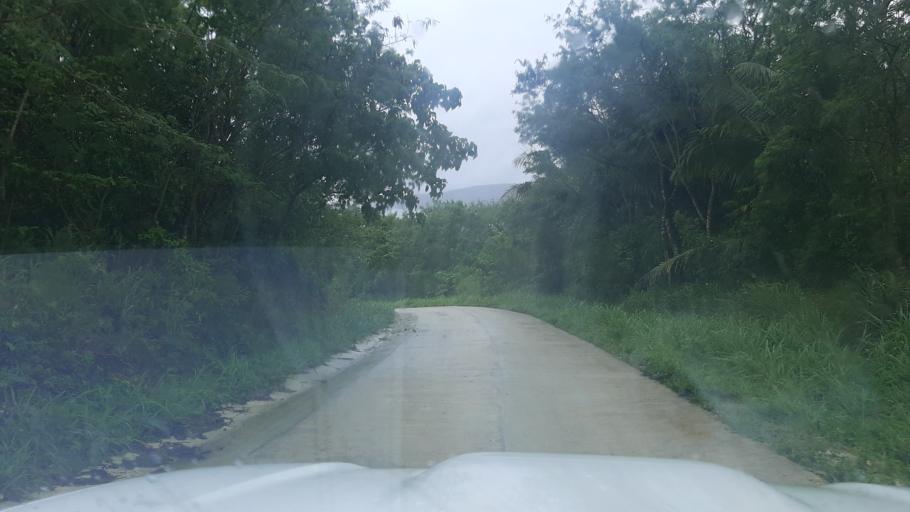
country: VU
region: Shefa
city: Port-Vila
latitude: -17.6374
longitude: 168.2120
